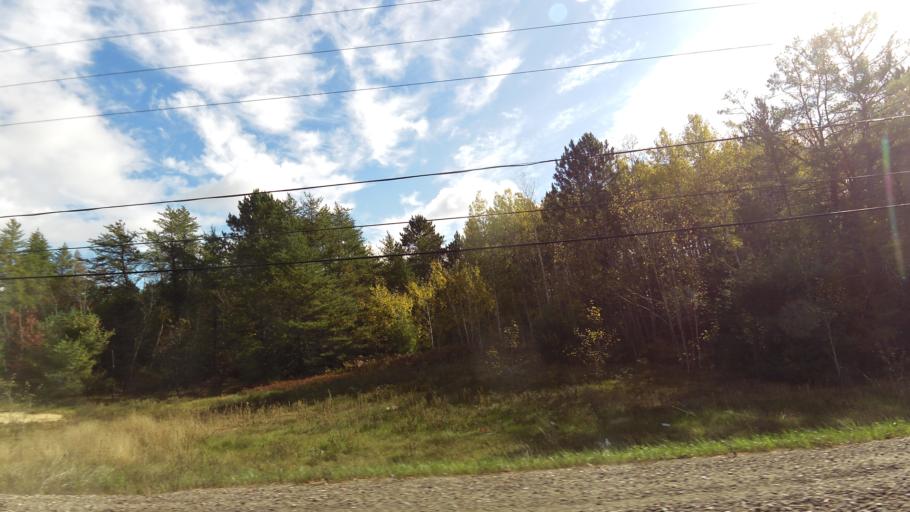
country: CA
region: Ontario
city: Deep River
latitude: 46.0617
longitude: -77.4740
